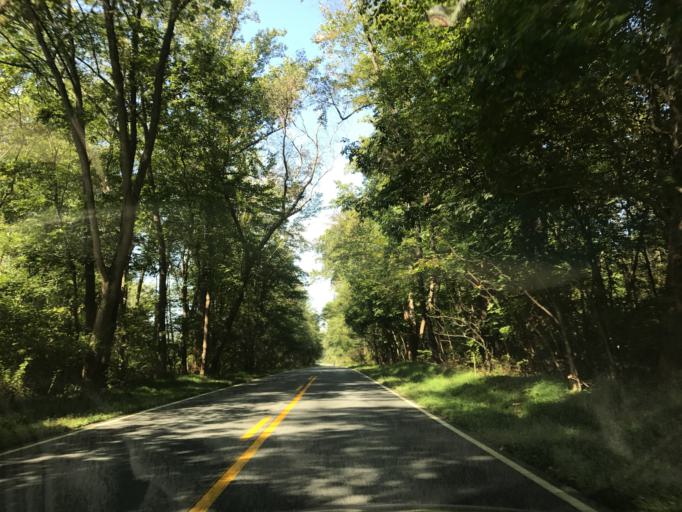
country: US
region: Maryland
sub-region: Cecil County
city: Rising Sun
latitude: 39.6522
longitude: -76.1533
